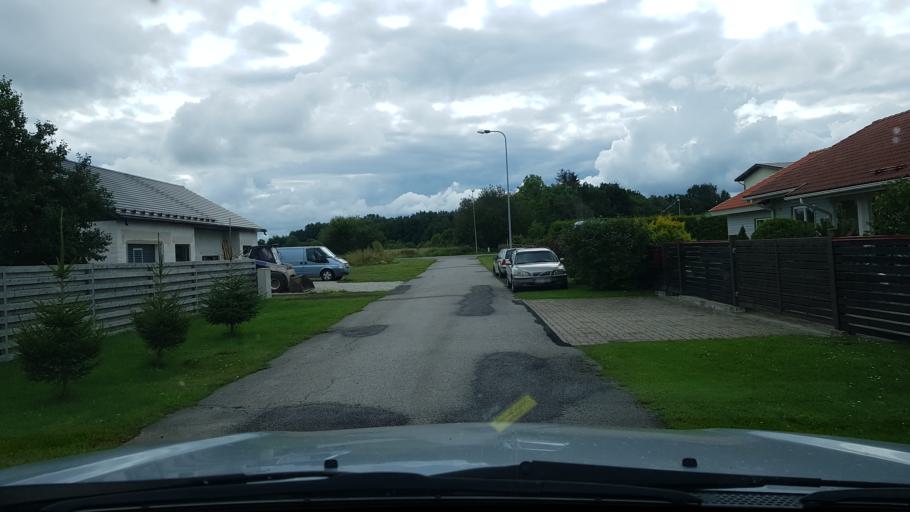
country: EE
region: Harju
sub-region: Rae vald
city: Vaida
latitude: 59.3174
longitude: 24.9474
